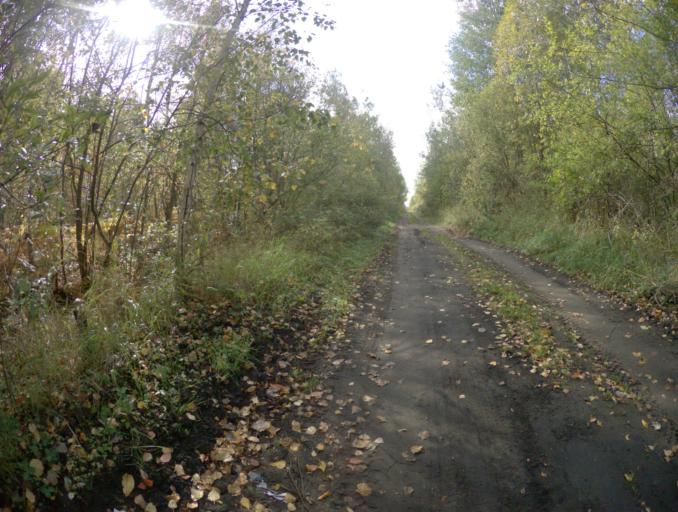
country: RU
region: Moskovskaya
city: Kerva
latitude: 55.7059
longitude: 39.5978
